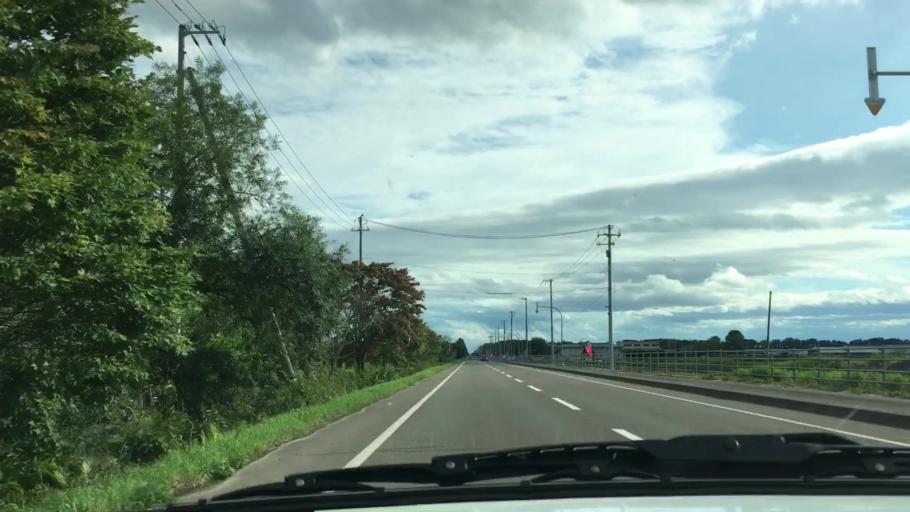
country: JP
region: Hokkaido
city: Otofuke
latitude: 43.2568
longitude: 143.3005
